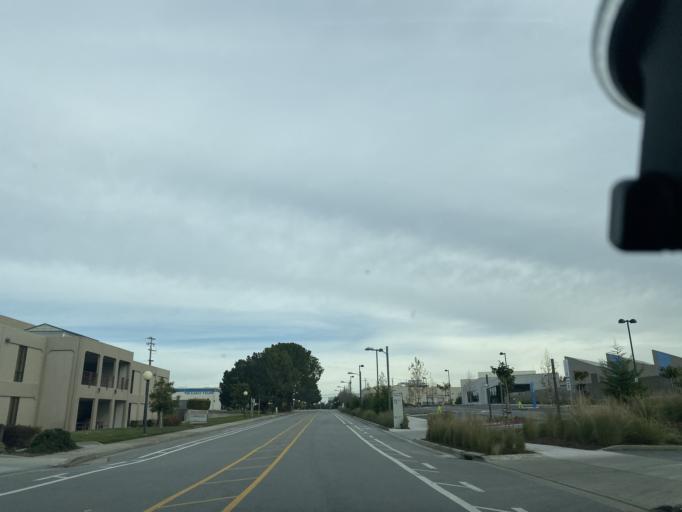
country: US
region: California
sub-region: San Mateo County
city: South San Francisco
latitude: 37.6526
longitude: -122.3917
